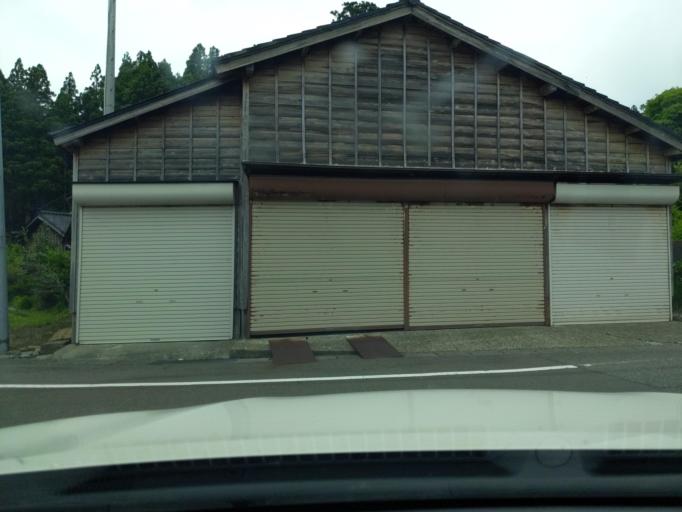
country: JP
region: Niigata
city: Kashiwazaki
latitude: 37.3439
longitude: 138.5858
